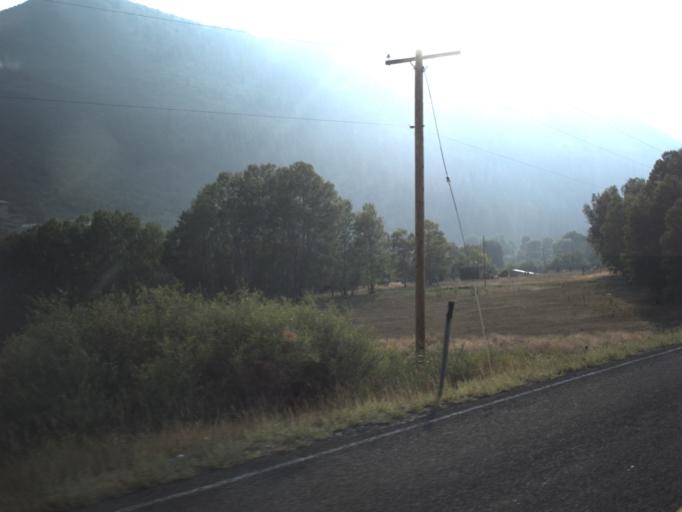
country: US
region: Utah
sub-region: Summit County
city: Francis
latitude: 40.6251
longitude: -111.2291
